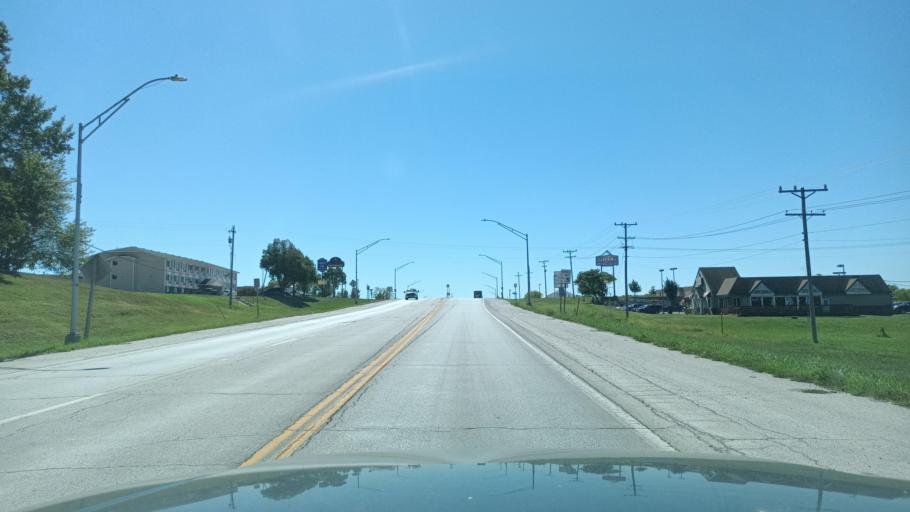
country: US
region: Missouri
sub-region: Adair County
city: Kirksville
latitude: 40.1725
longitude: -92.5720
